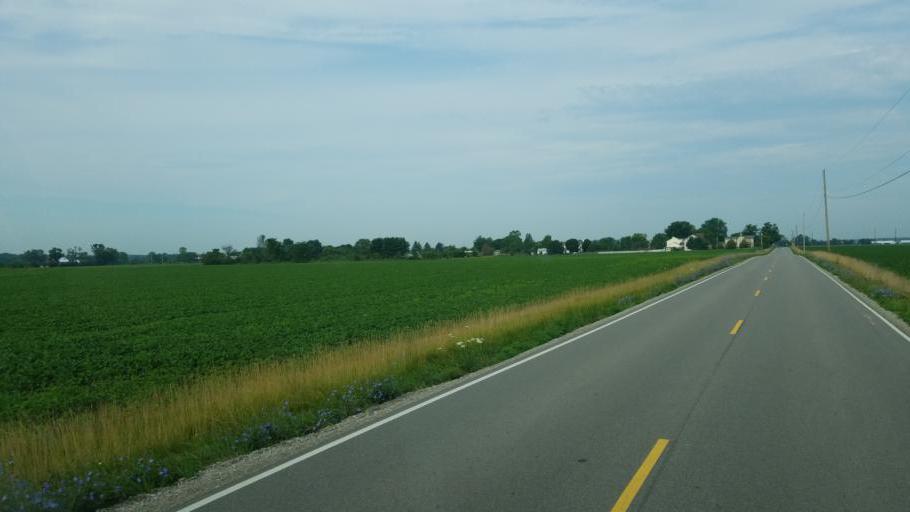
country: US
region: Ohio
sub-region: Union County
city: New California
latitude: 40.2170
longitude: -83.1616
